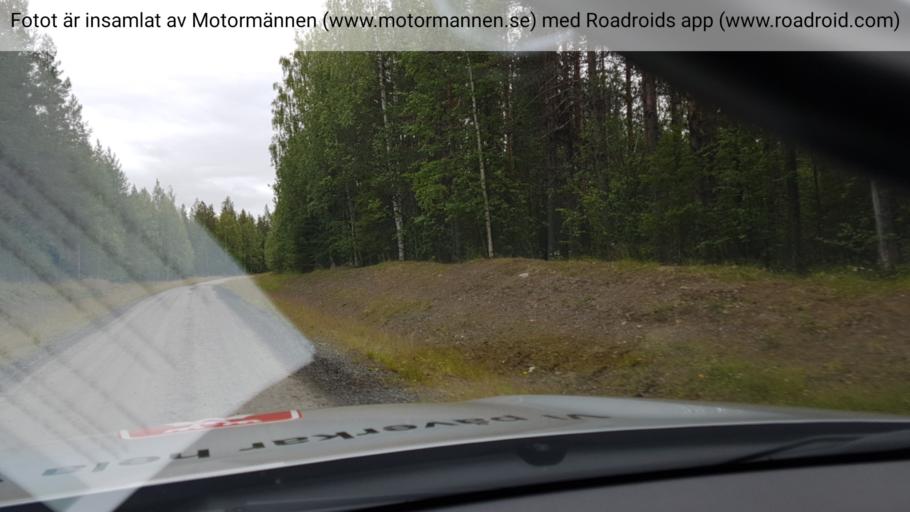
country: SE
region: Norrbotten
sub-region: Pajala Kommun
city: Pajala
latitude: 67.0038
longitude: 22.8572
